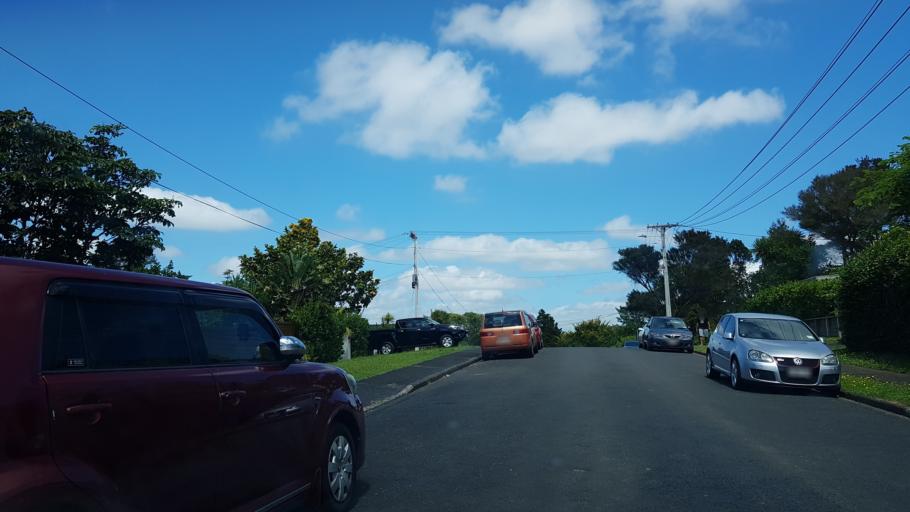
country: NZ
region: Auckland
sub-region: Auckland
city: North Shore
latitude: -36.7921
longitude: 174.7183
